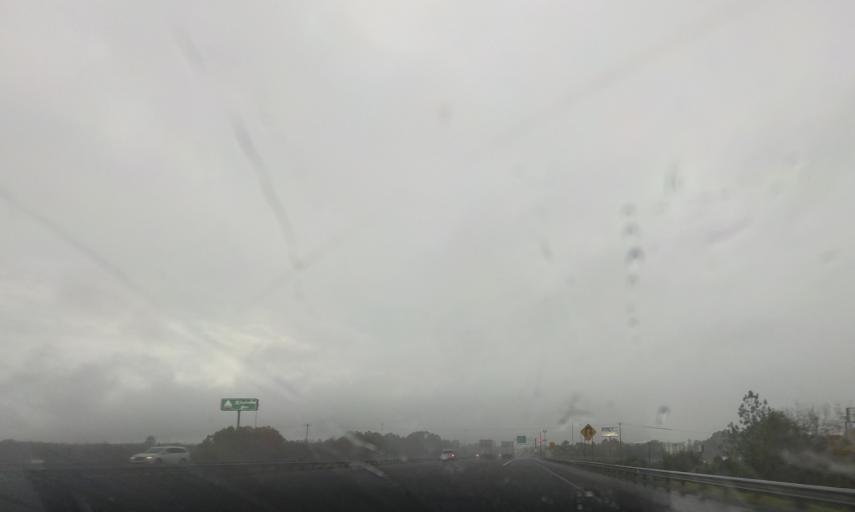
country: US
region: Georgia
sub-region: Lowndes County
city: Remerton
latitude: 30.8170
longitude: -83.3158
